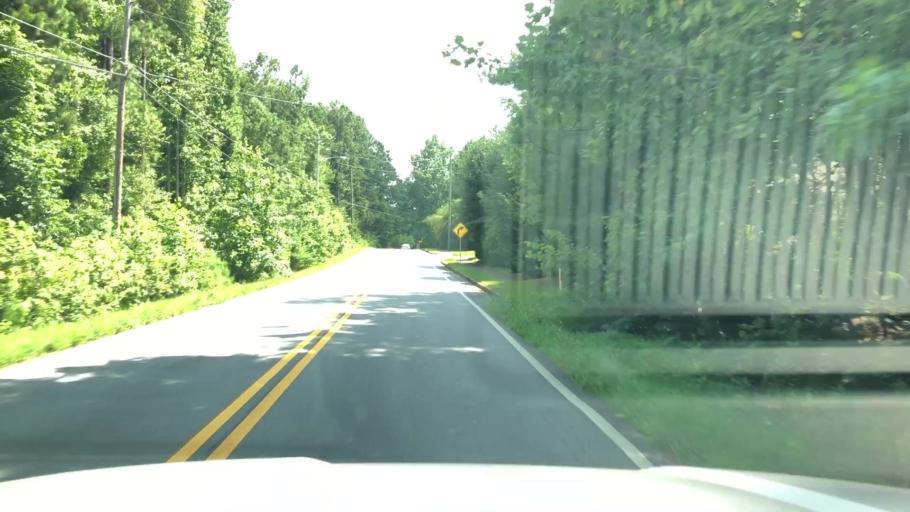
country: US
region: Georgia
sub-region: Paulding County
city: Hiram
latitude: 33.9520
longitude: -84.7263
